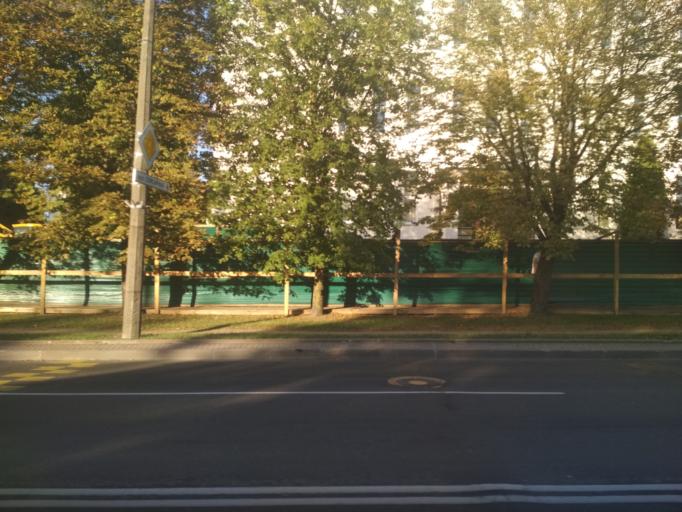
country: BY
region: Minsk
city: Minsk
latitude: 53.8998
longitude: 27.5853
